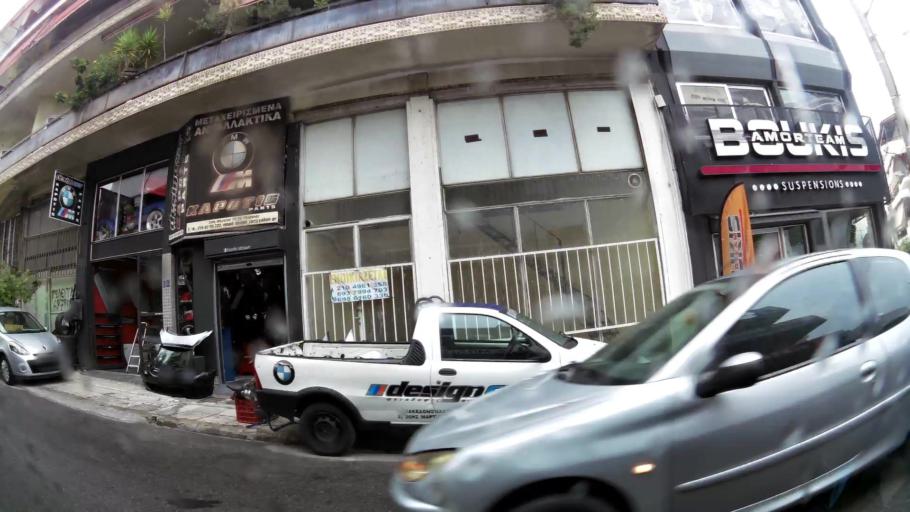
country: GR
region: Attica
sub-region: Nomos Piraios
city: Nikaia
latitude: 37.9574
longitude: 23.6496
